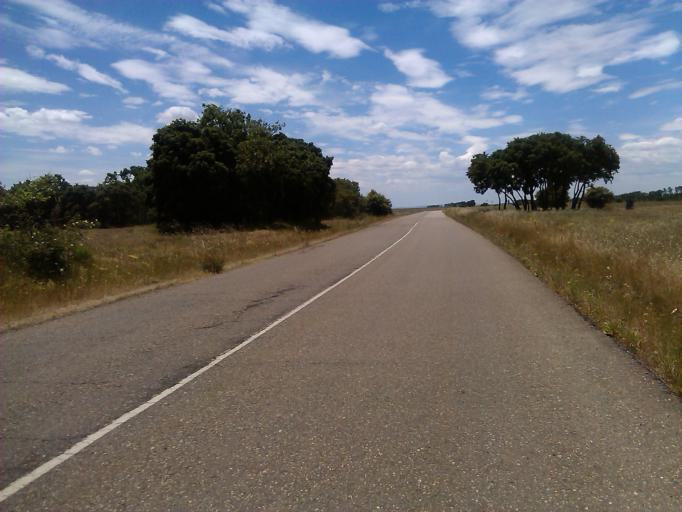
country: ES
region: Castille and Leon
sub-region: Provincia de Leon
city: Chozas de Abajo
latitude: 42.4957
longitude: -5.7076
